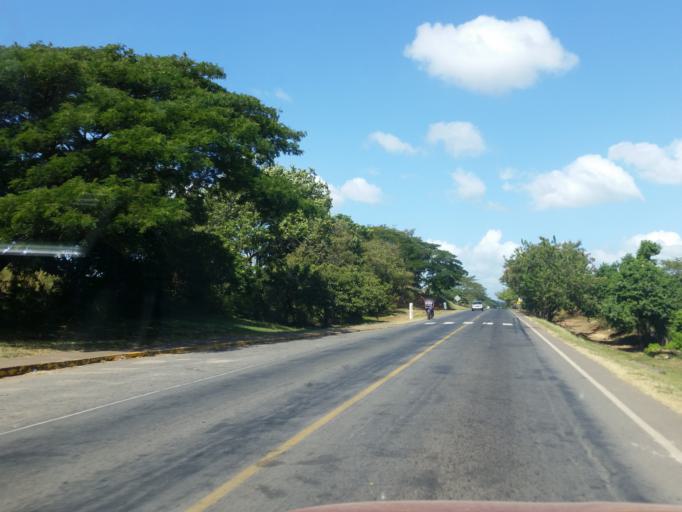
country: NI
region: Granada
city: Nandaime
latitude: 11.7289
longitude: -86.0145
